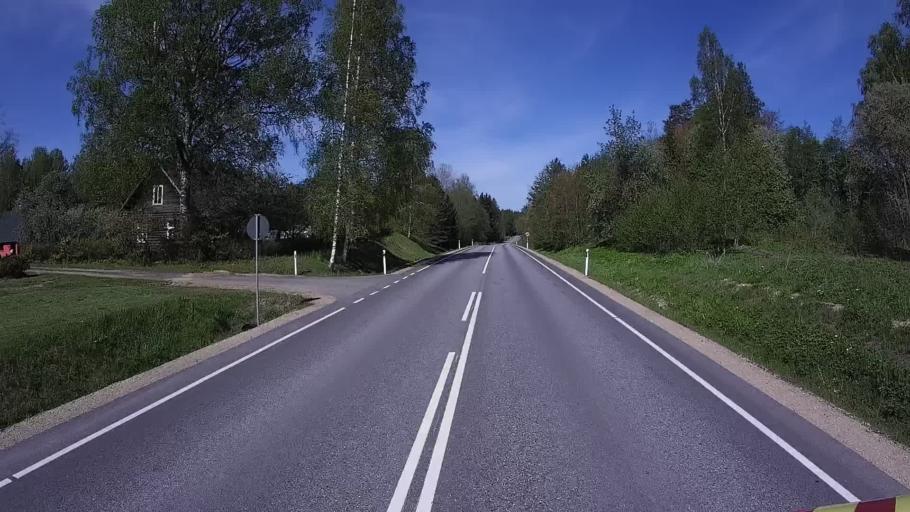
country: EE
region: Polvamaa
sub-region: Raepina vald
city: Rapina
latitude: 57.9806
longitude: 27.2773
